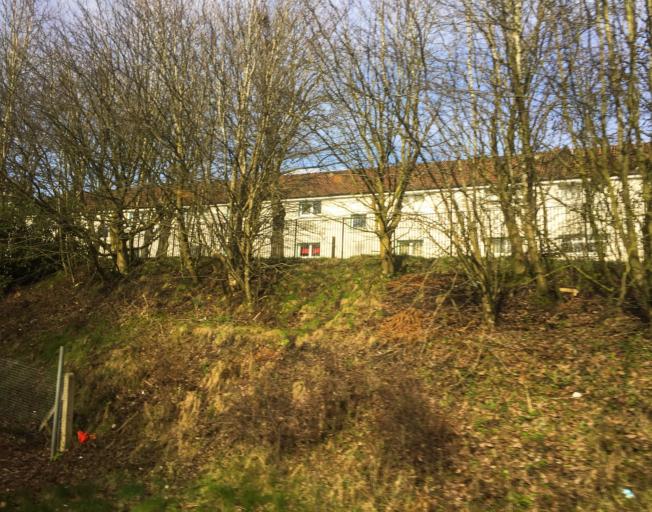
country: GB
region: Scotland
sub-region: Glasgow City
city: Glasgow
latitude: 55.8968
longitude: -4.2811
